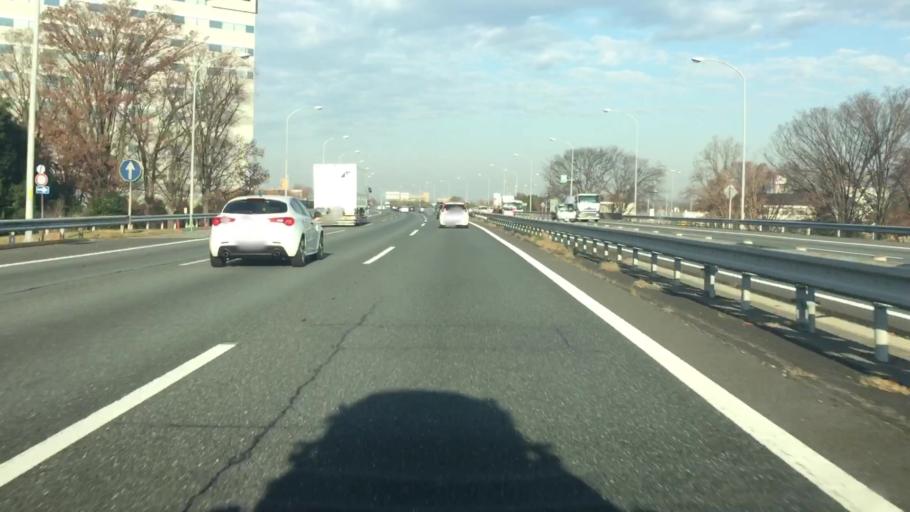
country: JP
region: Saitama
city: Sakado
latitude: 35.9458
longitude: 139.3989
